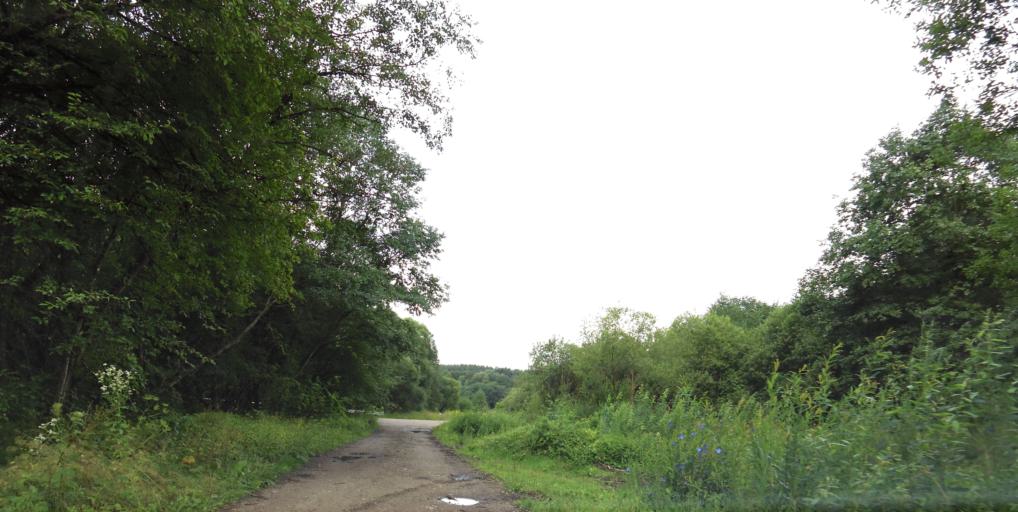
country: LT
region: Vilnius County
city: Pilaite
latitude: 54.6975
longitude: 25.1916
